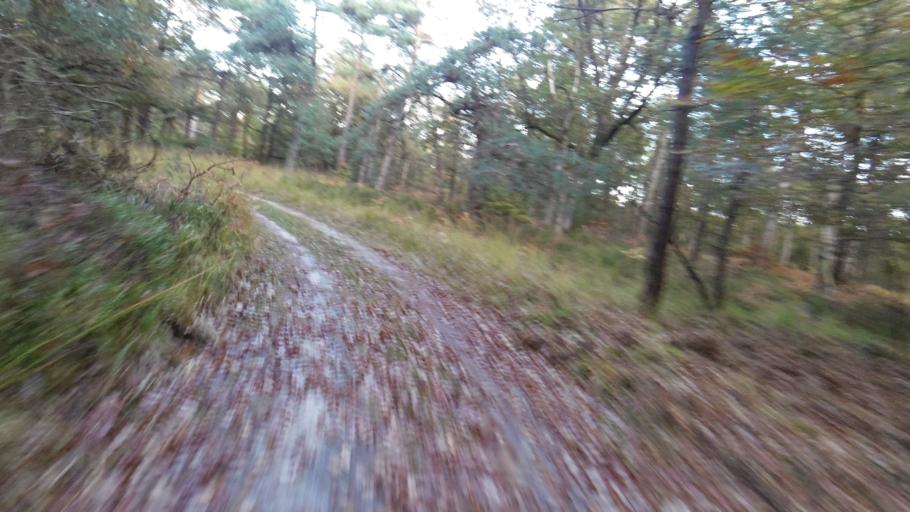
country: NL
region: Gelderland
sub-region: Gemeente Apeldoorn
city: Uddel
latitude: 52.2820
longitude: 5.8248
